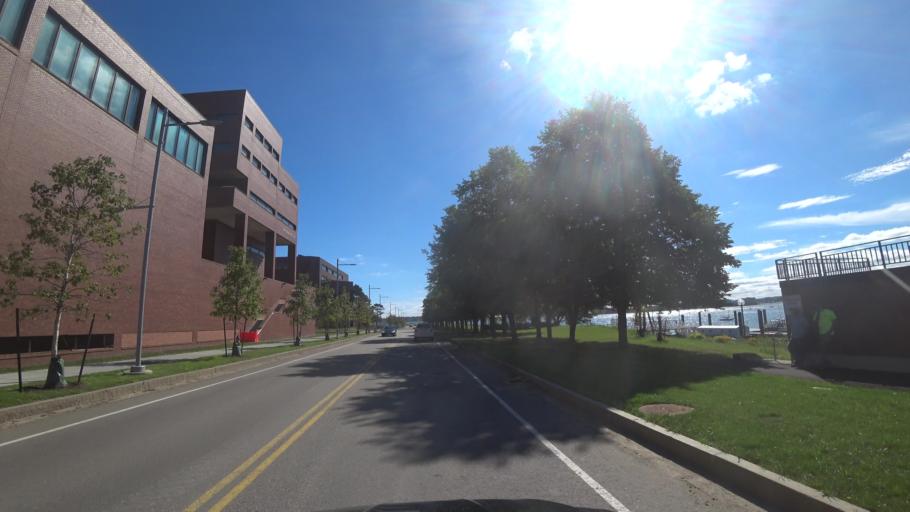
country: US
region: Massachusetts
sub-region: Suffolk County
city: South Boston
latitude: 42.3125
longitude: -71.0407
